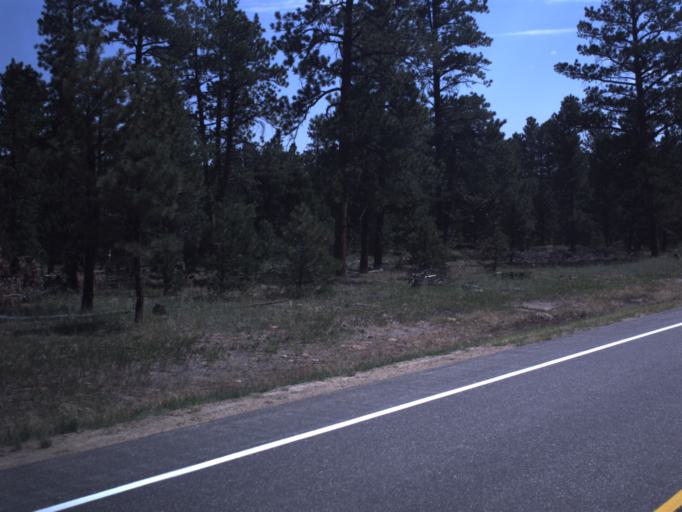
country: US
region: Utah
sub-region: Daggett County
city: Manila
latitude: 40.8526
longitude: -109.5991
